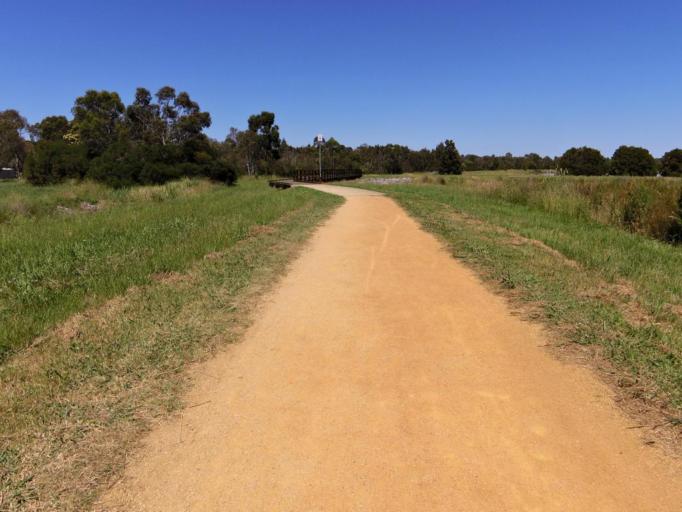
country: AU
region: Victoria
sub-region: Casey
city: Endeavour Hills
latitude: -37.9922
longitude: 145.2731
